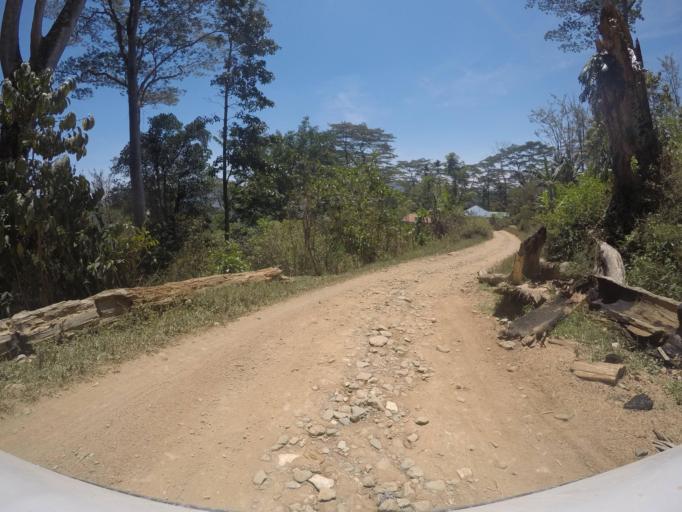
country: TL
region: Ermera
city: Gleno
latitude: -8.7382
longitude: 125.4065
